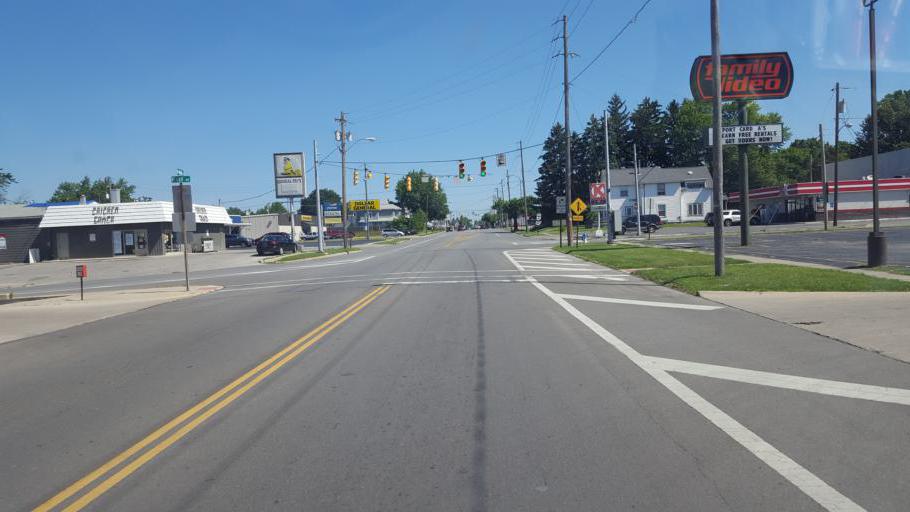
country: US
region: Ohio
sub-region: Marion County
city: Marion
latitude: 40.5979
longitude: -83.1295
